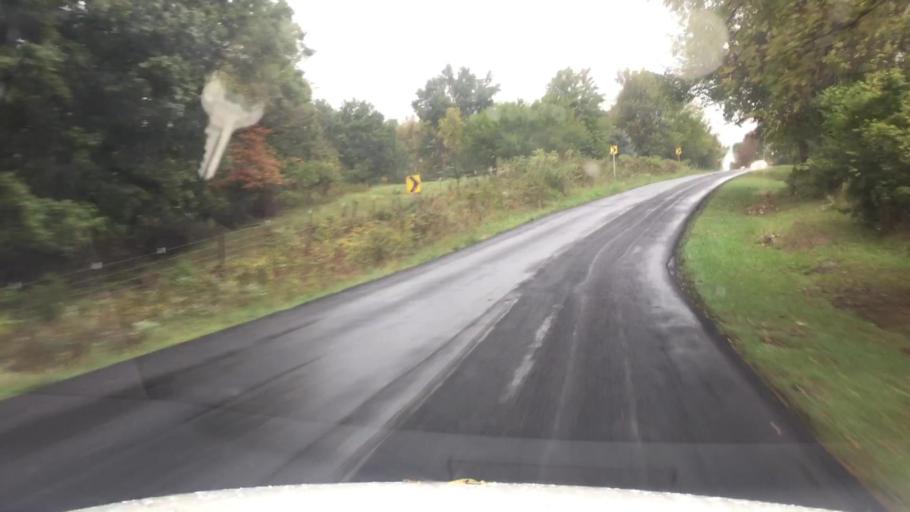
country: US
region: Missouri
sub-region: Boone County
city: Columbia
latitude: 38.9288
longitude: -92.4686
